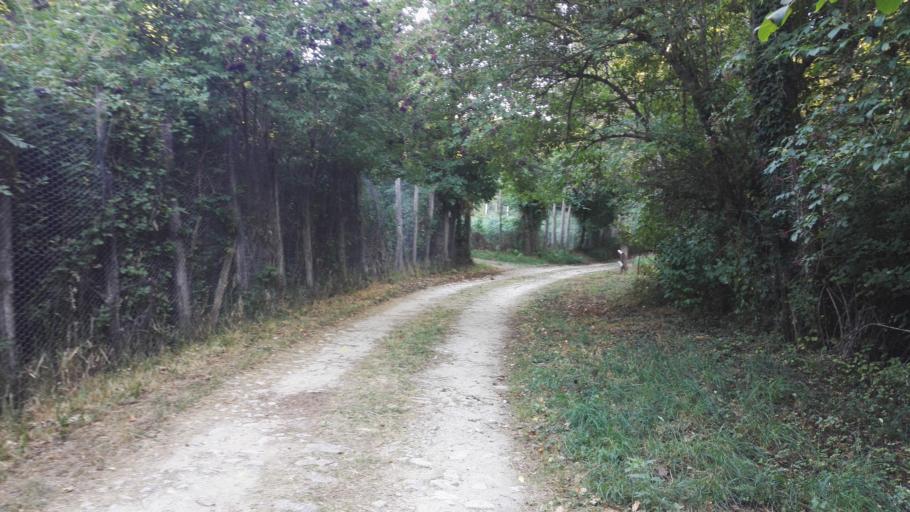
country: IT
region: Calabria
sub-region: Provincia di Vibo-Valentia
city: Mongiana
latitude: 38.5203
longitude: 16.3076
